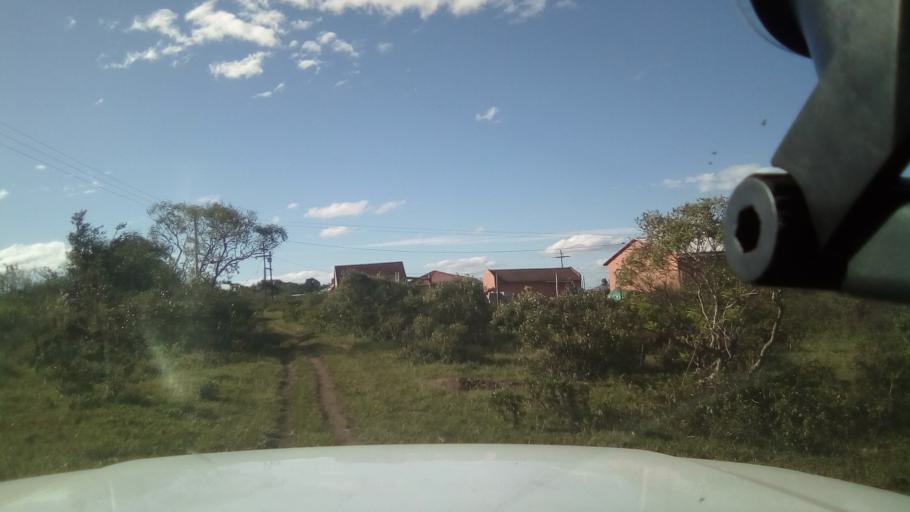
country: ZA
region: Eastern Cape
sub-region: Amathole District Municipality
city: Komga
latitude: -32.7756
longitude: 27.9322
